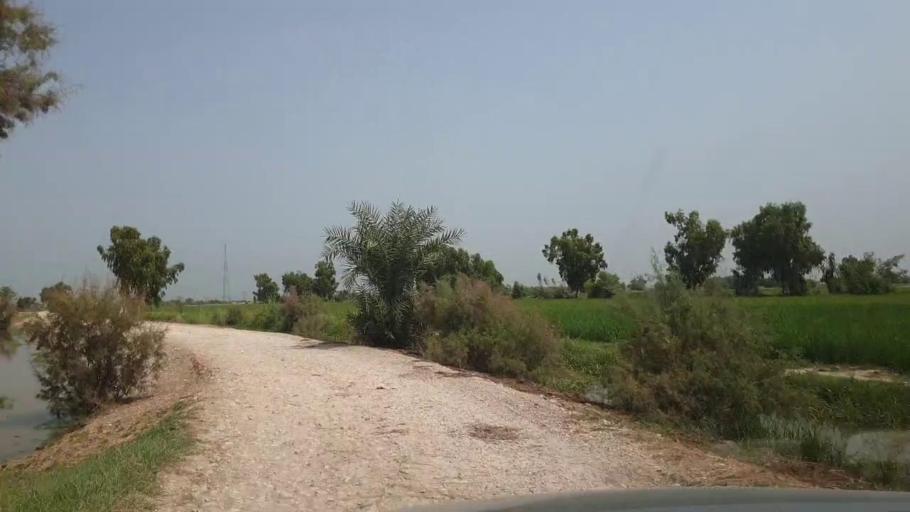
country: PK
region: Sindh
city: Madeji
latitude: 27.7976
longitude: 68.5325
